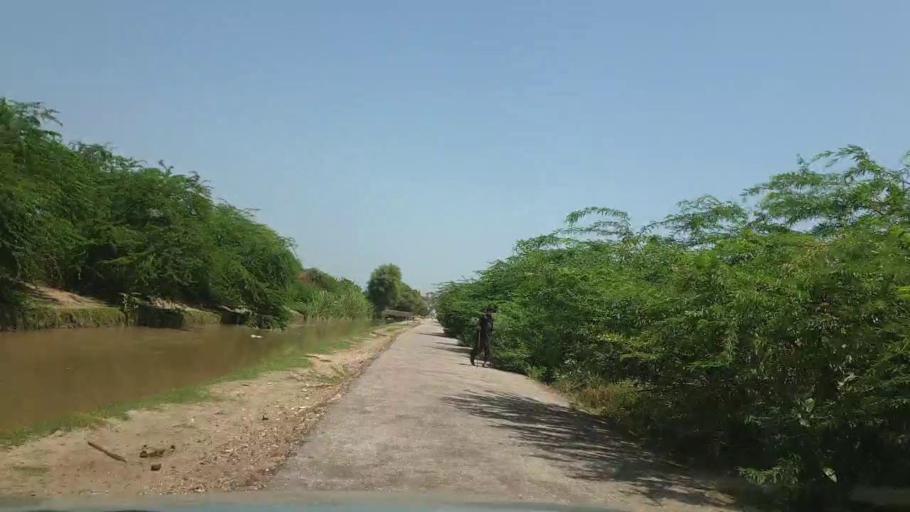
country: PK
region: Sindh
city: Rohri
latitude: 27.6275
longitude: 69.0981
